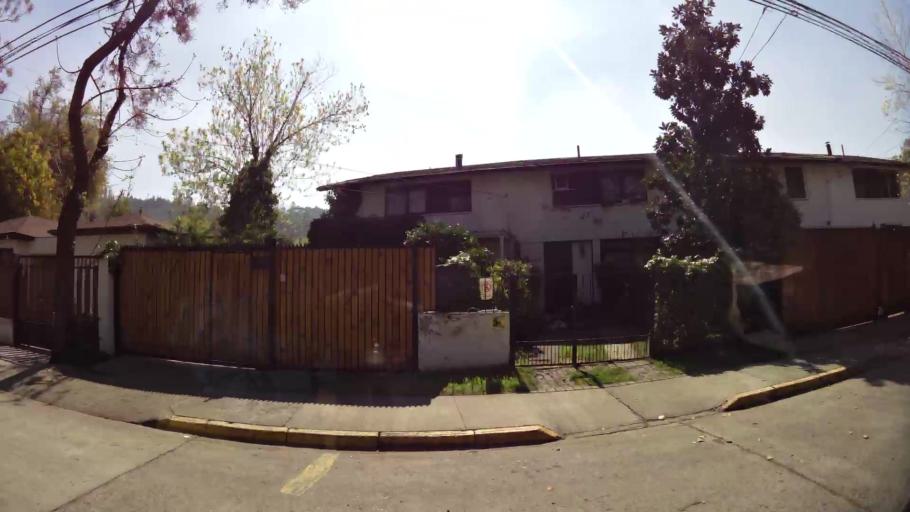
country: CL
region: Santiago Metropolitan
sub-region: Provincia de Santiago
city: Santiago
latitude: -33.4184
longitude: -70.6163
